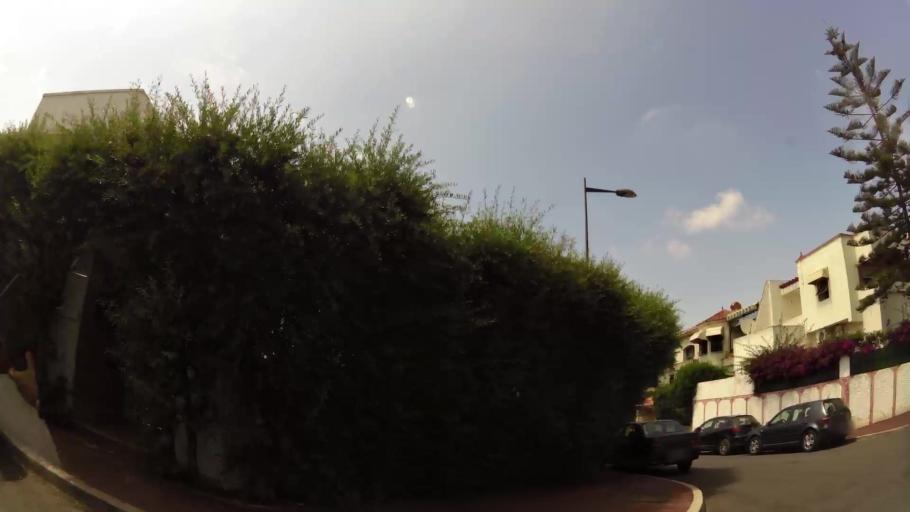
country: MA
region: Rabat-Sale-Zemmour-Zaer
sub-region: Skhirate-Temara
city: Temara
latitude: 33.9641
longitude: -6.8773
